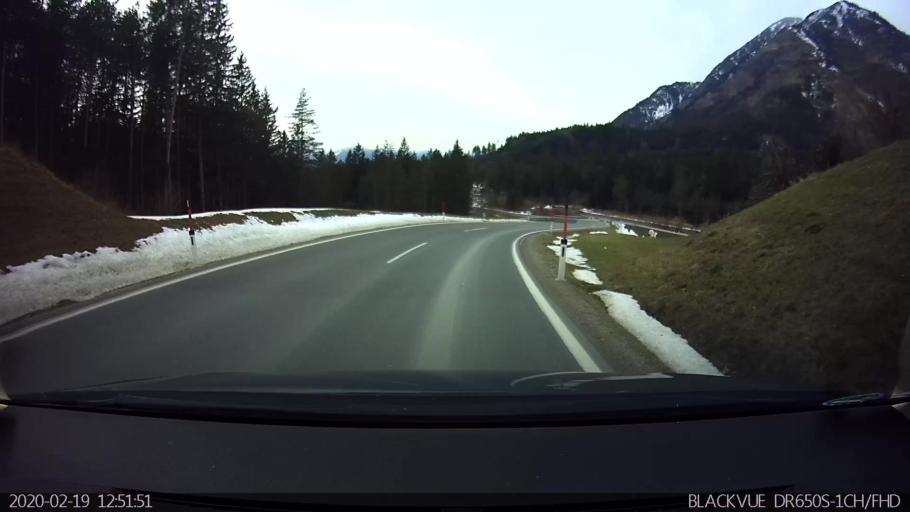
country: AT
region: Tyrol
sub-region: Politischer Bezirk Innsbruck Land
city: Hall in Tirol
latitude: 47.3115
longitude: 11.5288
